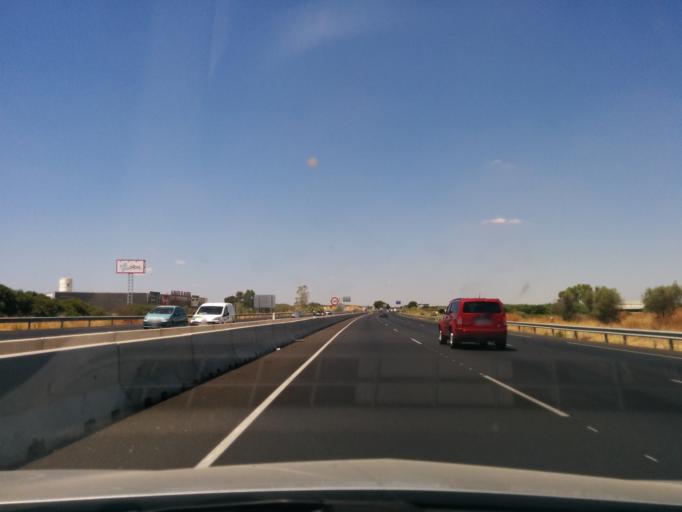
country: ES
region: Andalusia
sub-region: Provincia de Sevilla
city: Umbrete
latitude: 37.3589
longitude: -6.1485
